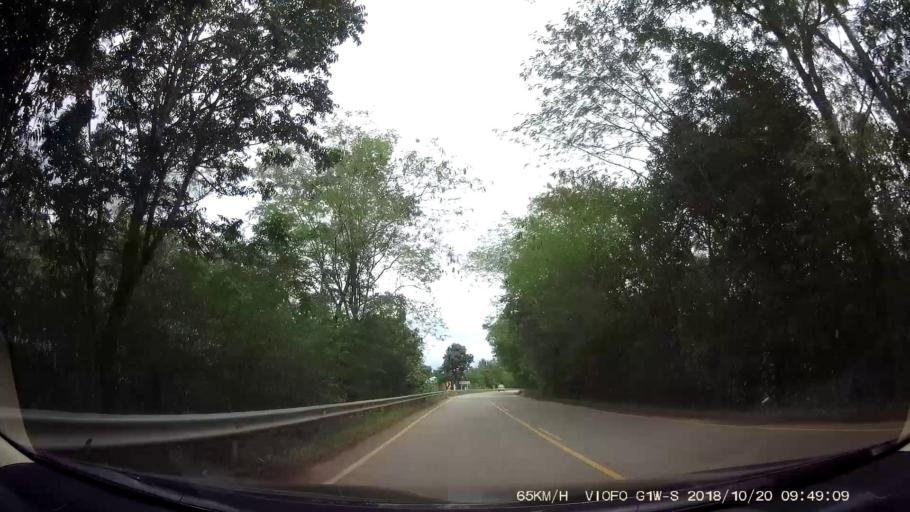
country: TH
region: Chaiyaphum
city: Khon San
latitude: 16.5167
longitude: 101.9067
